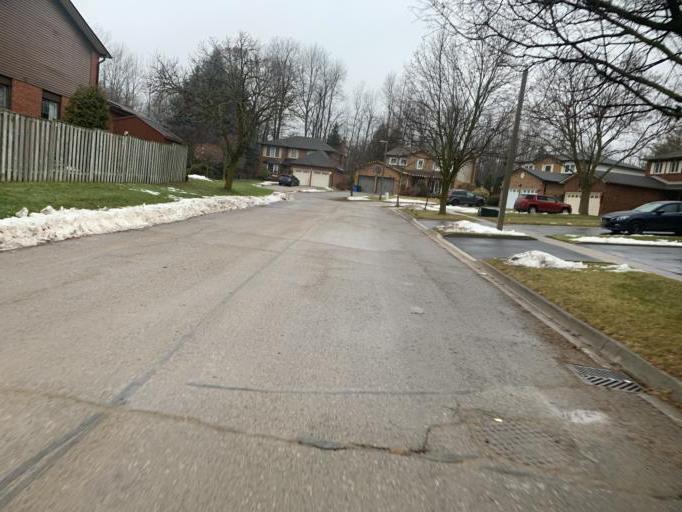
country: CA
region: Ontario
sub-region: Halton
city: Milton
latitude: 43.6601
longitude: -79.9280
